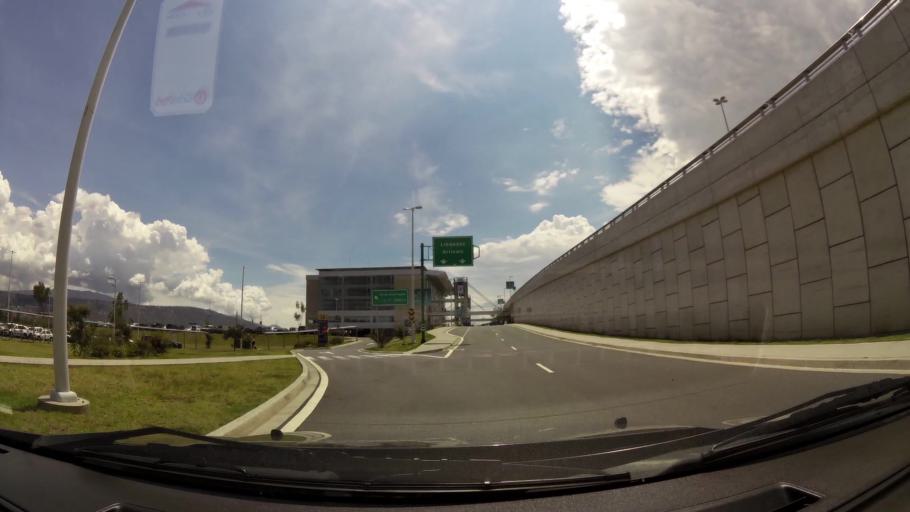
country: EC
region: Pichincha
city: Quito
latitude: -0.1261
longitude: -78.3610
